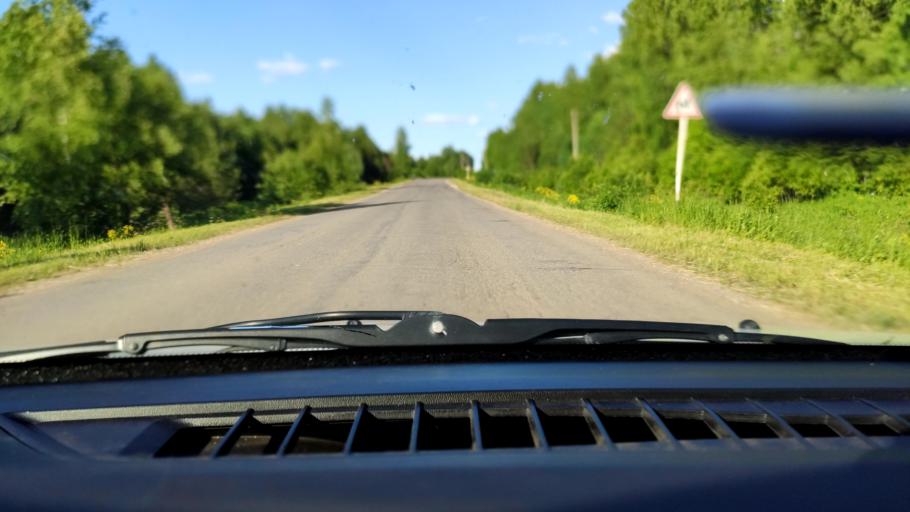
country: RU
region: Perm
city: Orda
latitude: 57.1329
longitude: 56.7052
